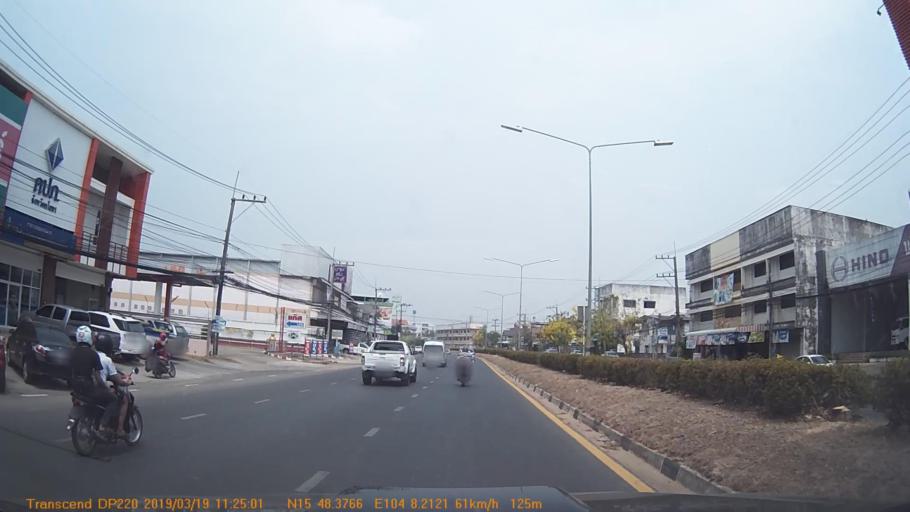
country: TH
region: Yasothon
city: Yasothon
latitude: 15.8064
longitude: 104.1368
